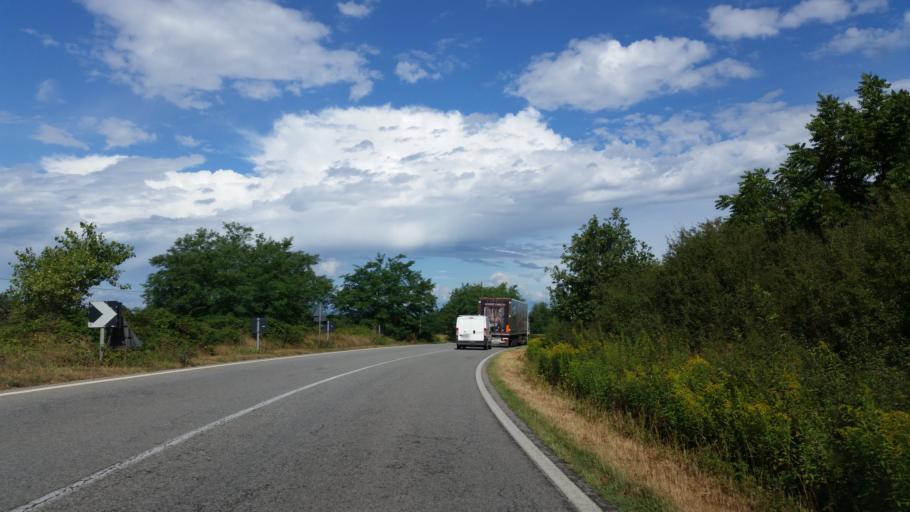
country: IT
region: Piedmont
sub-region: Provincia di Torino
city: Pralormo
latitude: 44.8365
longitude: 7.9170
